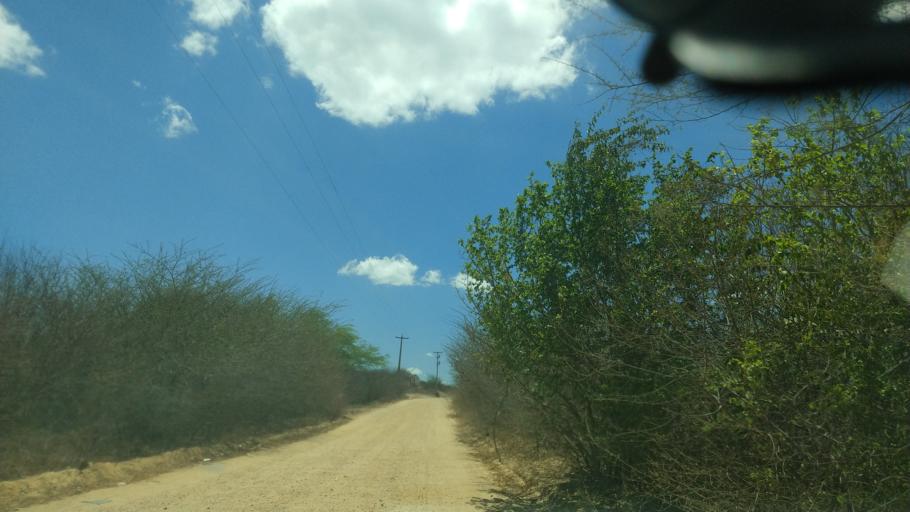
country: BR
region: Rio Grande do Norte
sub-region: Cerro Cora
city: Cerro Cora
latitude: -6.0205
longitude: -36.3316
